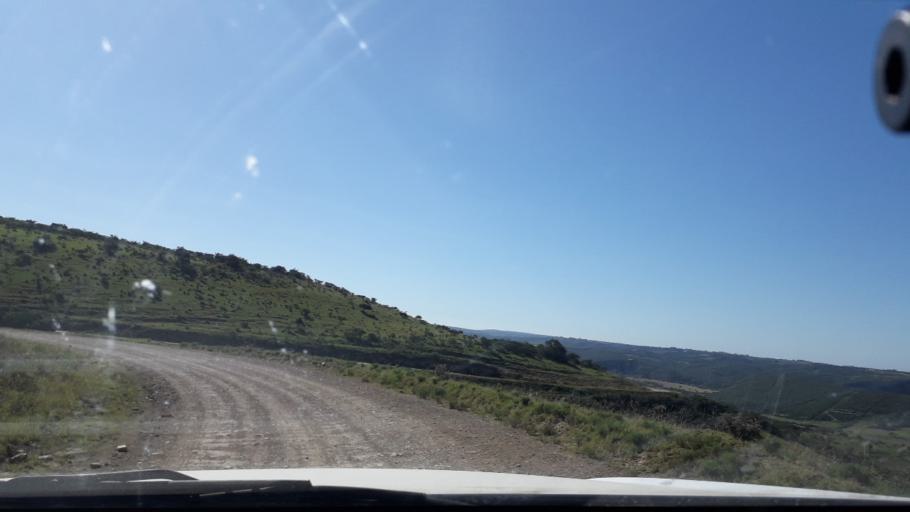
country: ZA
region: Eastern Cape
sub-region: Amathole District Municipality
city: Komga
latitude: -32.7876
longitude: 27.9536
